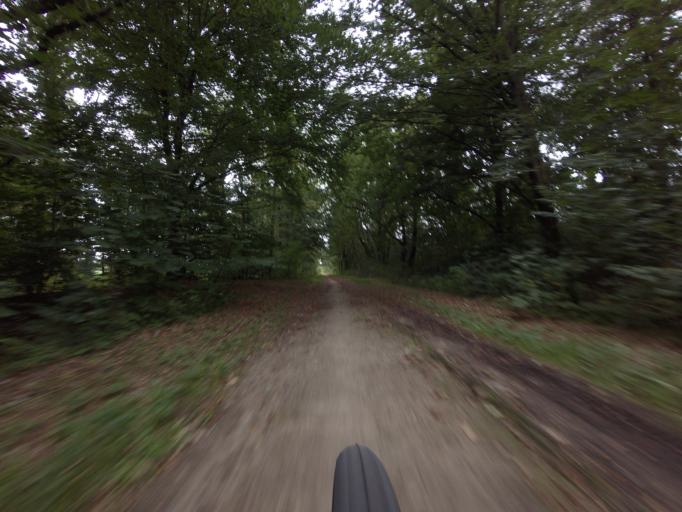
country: DK
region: Central Jutland
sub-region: Ikast-Brande Kommune
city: Brande
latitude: 55.9158
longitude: 9.0982
